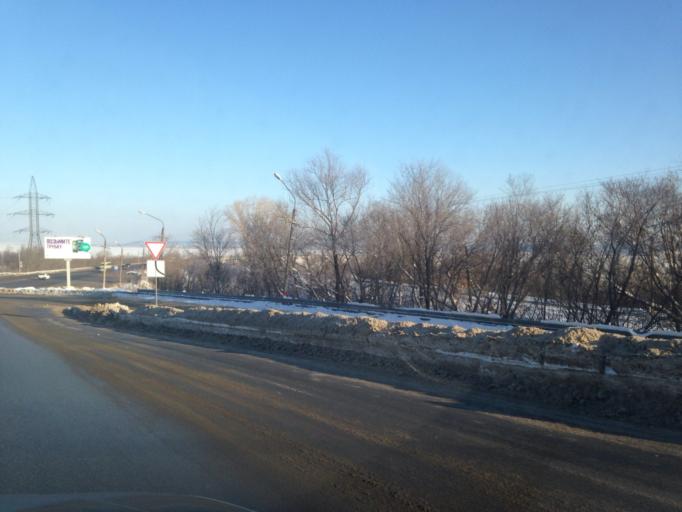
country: RU
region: Ulyanovsk
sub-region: Ulyanovskiy Rayon
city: Ulyanovsk
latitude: 54.3098
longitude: 48.4105
